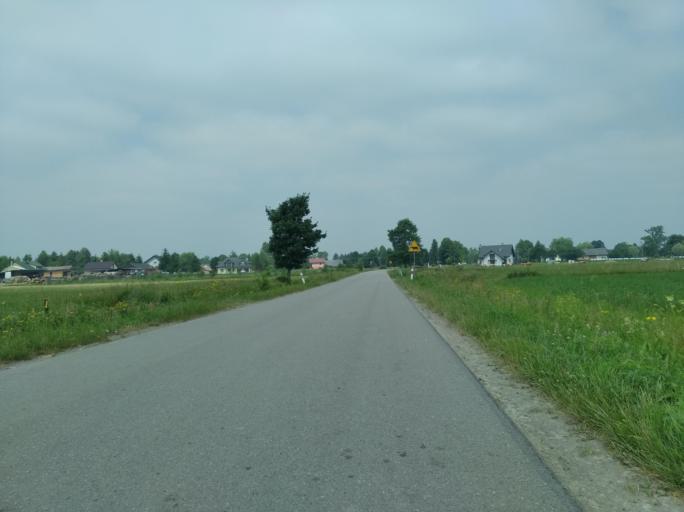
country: PL
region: Subcarpathian Voivodeship
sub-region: Powiat sanocki
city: Besko
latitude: 49.6143
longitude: 21.9480
